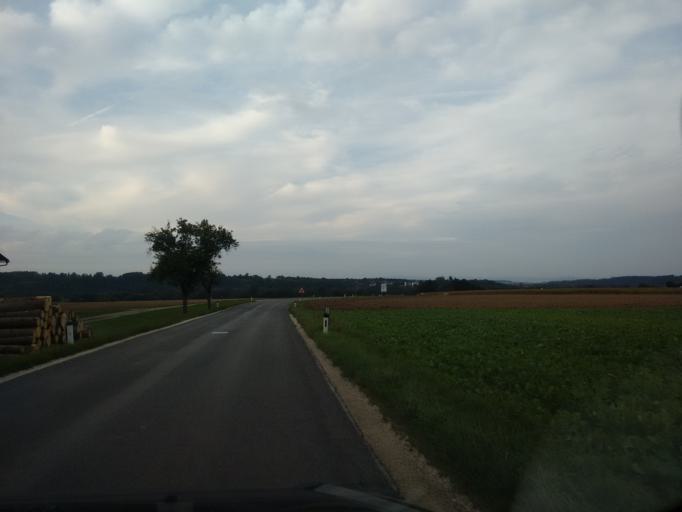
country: AT
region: Upper Austria
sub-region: Politischer Bezirk Steyr-Land
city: Pfarrkirchen bei Bad Hall
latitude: 48.0570
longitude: 14.1759
